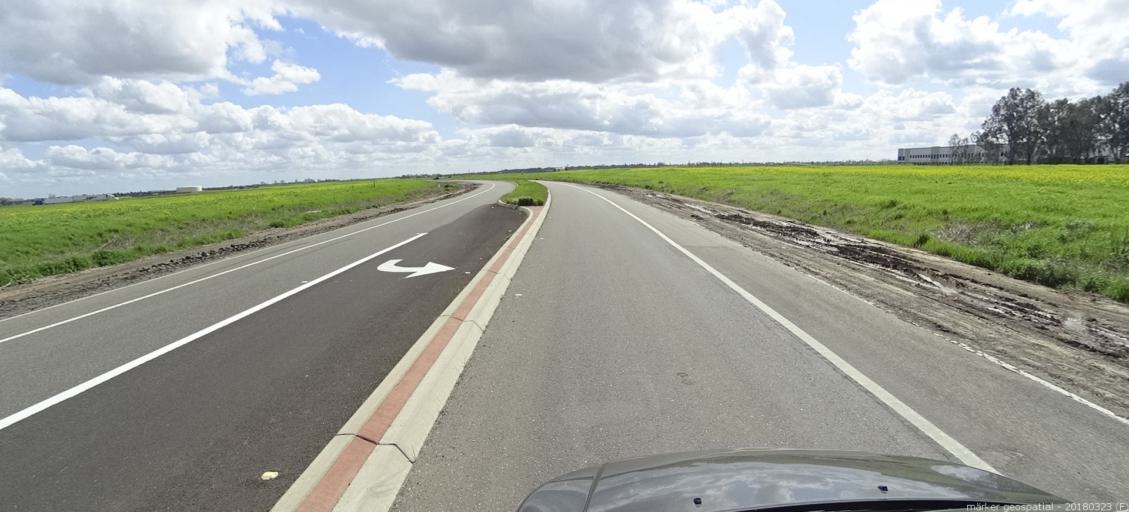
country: US
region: California
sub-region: Sacramento County
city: Elverta
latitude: 38.6852
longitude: -121.5697
